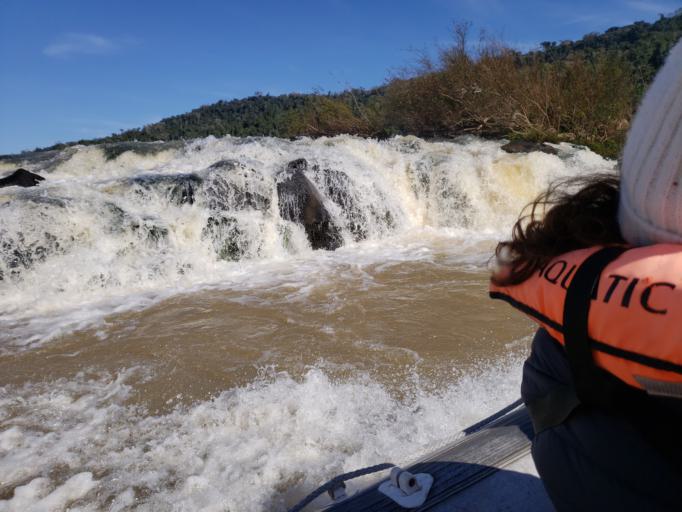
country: BR
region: Rio Grande do Sul
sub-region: Tres Passos
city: Tres Passos
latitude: -27.1454
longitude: -53.8869
